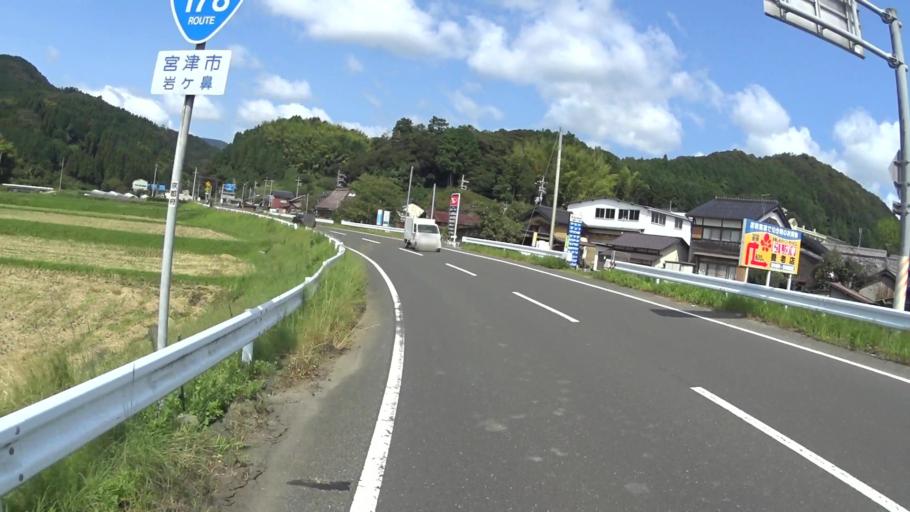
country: JP
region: Kyoto
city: Miyazu
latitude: 35.6570
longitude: 135.2586
